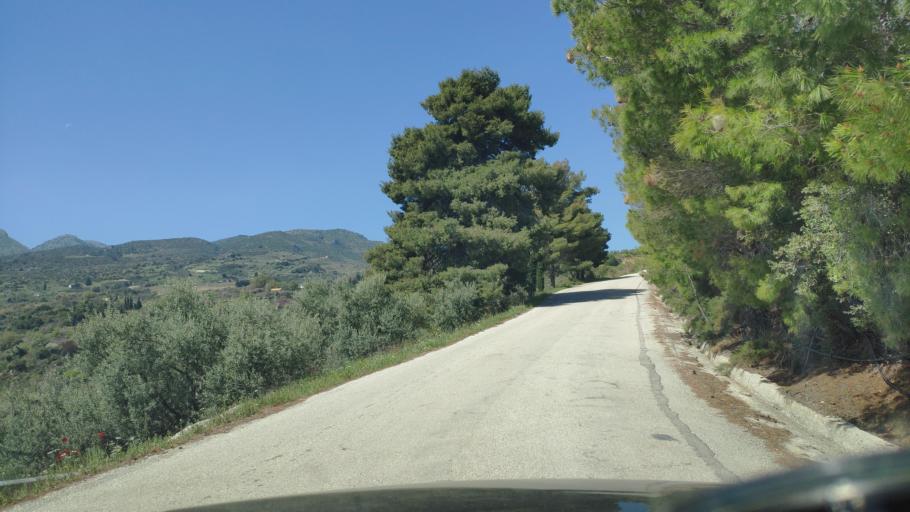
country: GR
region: West Greece
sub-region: Nomos Achaias
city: Akrata
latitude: 38.1125
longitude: 22.3254
